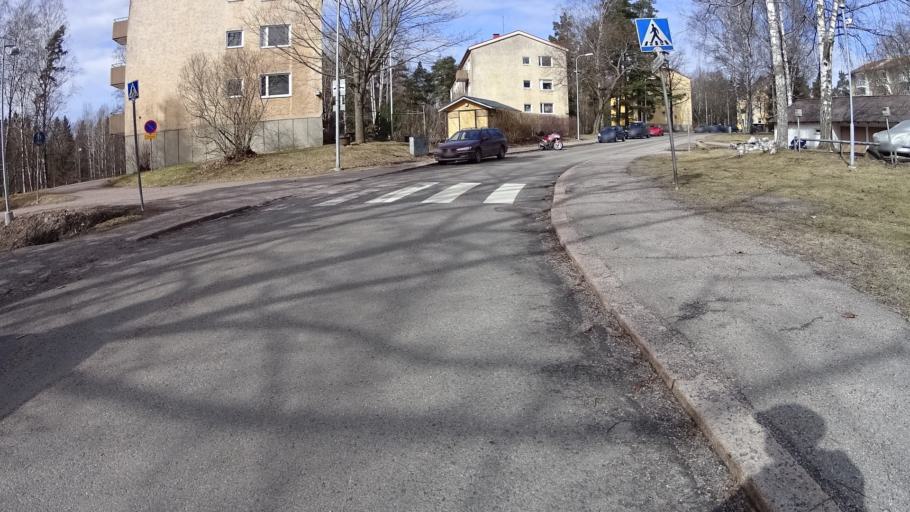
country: FI
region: Uusimaa
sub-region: Helsinki
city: Teekkarikylae
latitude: 60.2265
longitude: 24.8879
